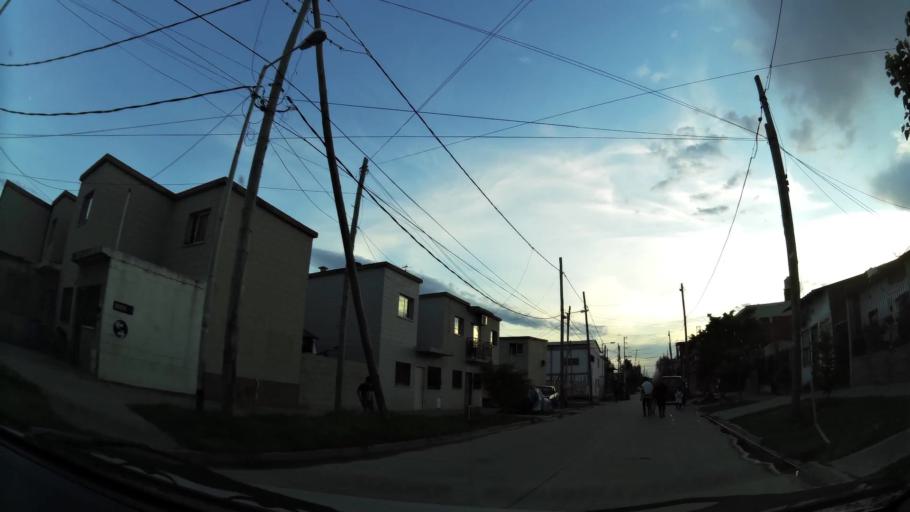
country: AR
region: Buenos Aires
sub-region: Partido de Avellaneda
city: Avellaneda
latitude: -34.6810
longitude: -58.3286
